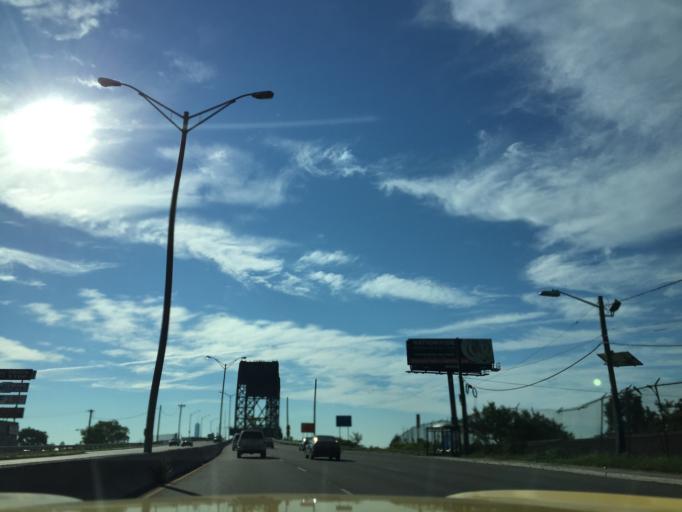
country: US
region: New Jersey
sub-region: Hudson County
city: Jersey City
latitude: 40.7287
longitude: -74.1040
